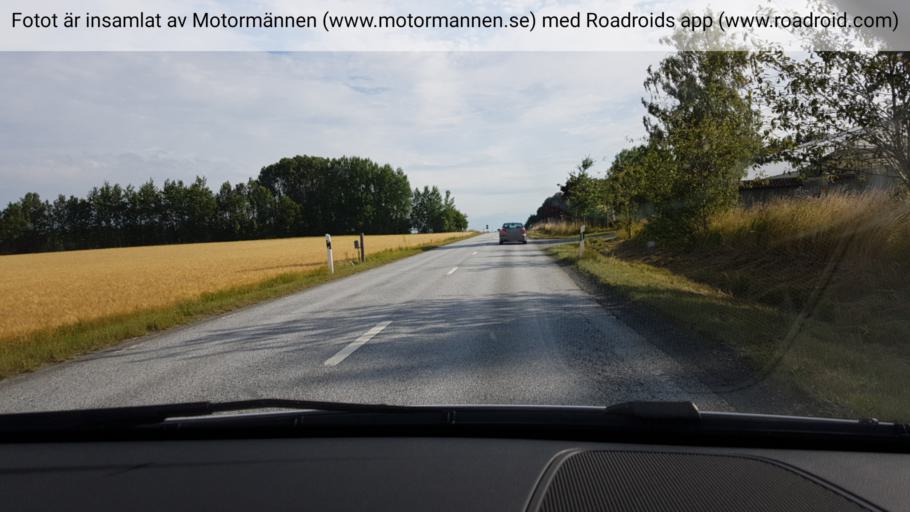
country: SE
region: Stockholm
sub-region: Norrtalje Kommun
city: Norrtalje
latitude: 59.9128
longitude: 18.7054
